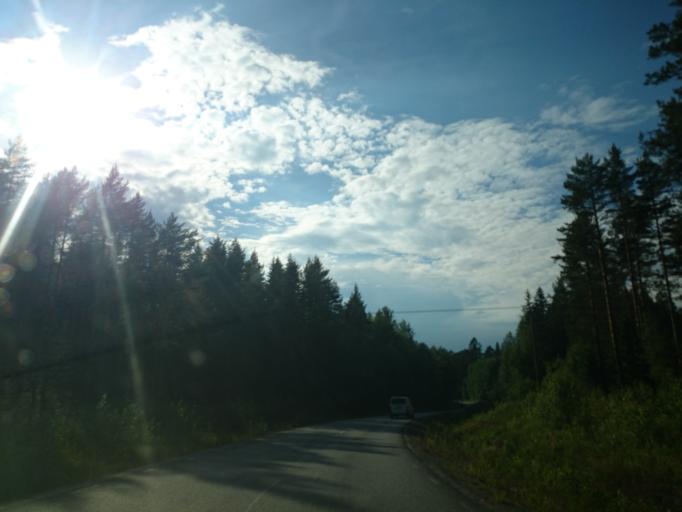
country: SE
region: Vaesternorrland
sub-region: Timra Kommun
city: Bergeforsen
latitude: 62.5541
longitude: 17.4041
